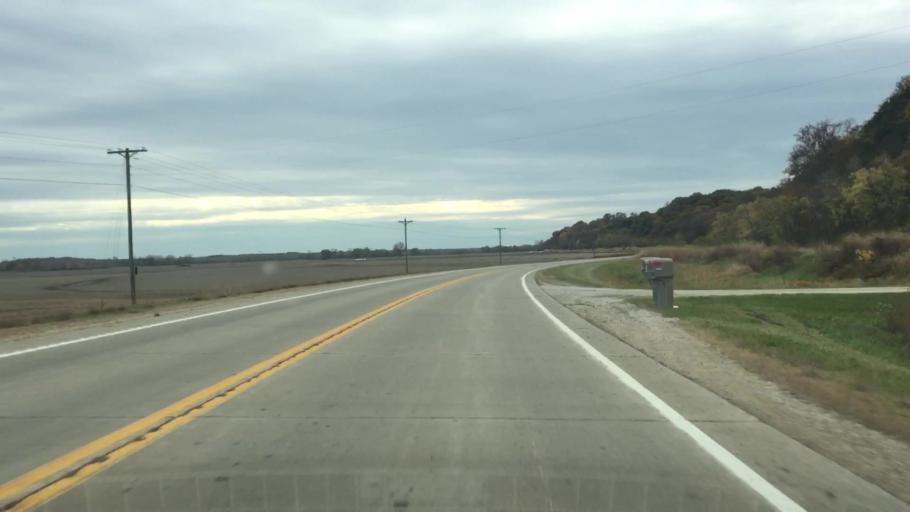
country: US
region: Missouri
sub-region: Callaway County
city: Holts Summit
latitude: 38.5874
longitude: -92.0316
